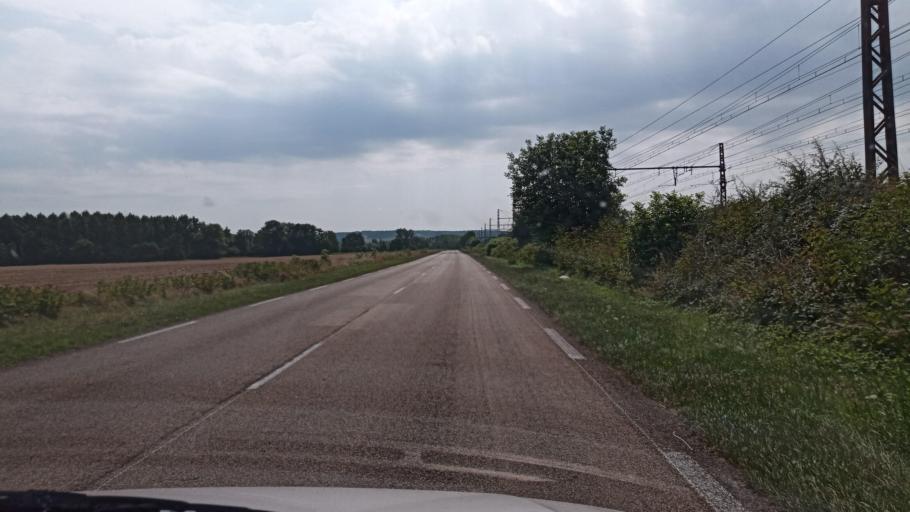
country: FR
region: Bourgogne
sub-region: Departement de l'Yonne
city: Villeneuve-sur-Yonne
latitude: 48.1038
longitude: 3.2713
